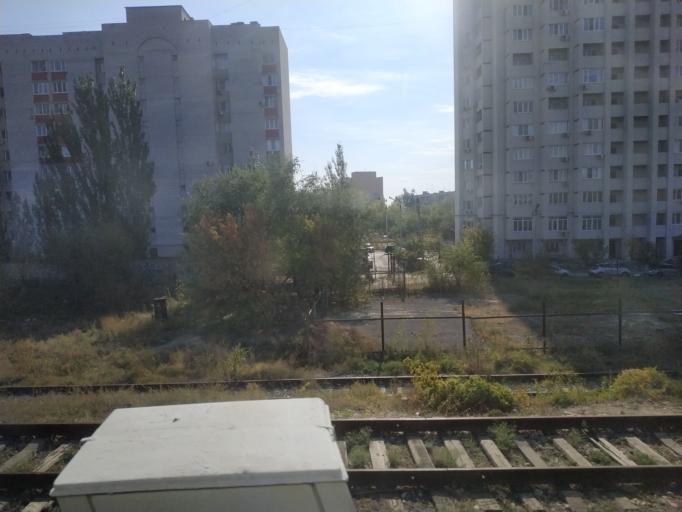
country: RU
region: Volgograd
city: Volgograd
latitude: 48.7315
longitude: 44.5326
